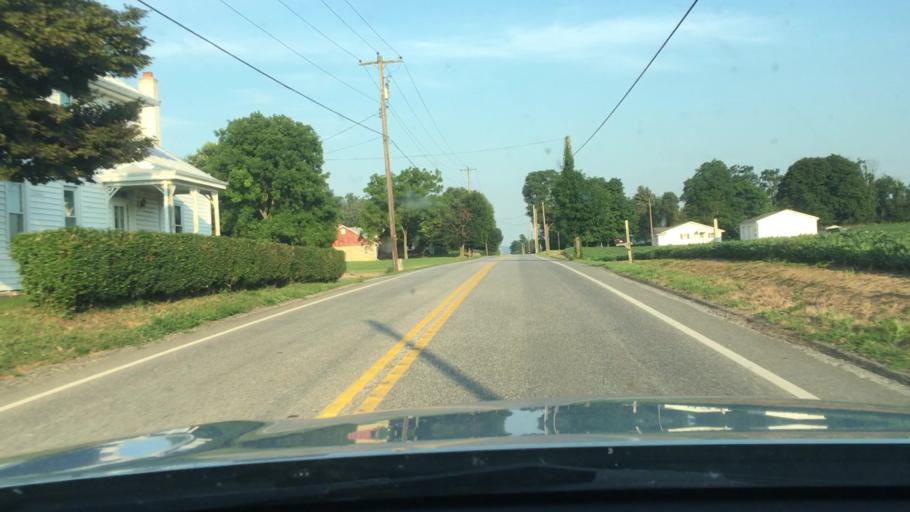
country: US
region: Pennsylvania
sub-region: Cumberland County
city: Boiling Springs
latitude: 40.1696
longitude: -77.1139
